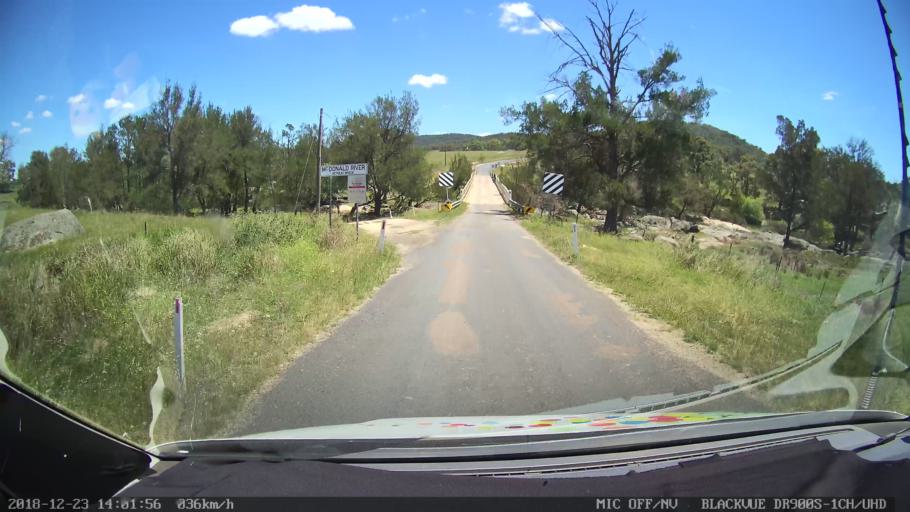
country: AU
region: New South Wales
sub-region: Tamworth Municipality
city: Manilla
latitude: -30.6226
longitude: 151.1100
